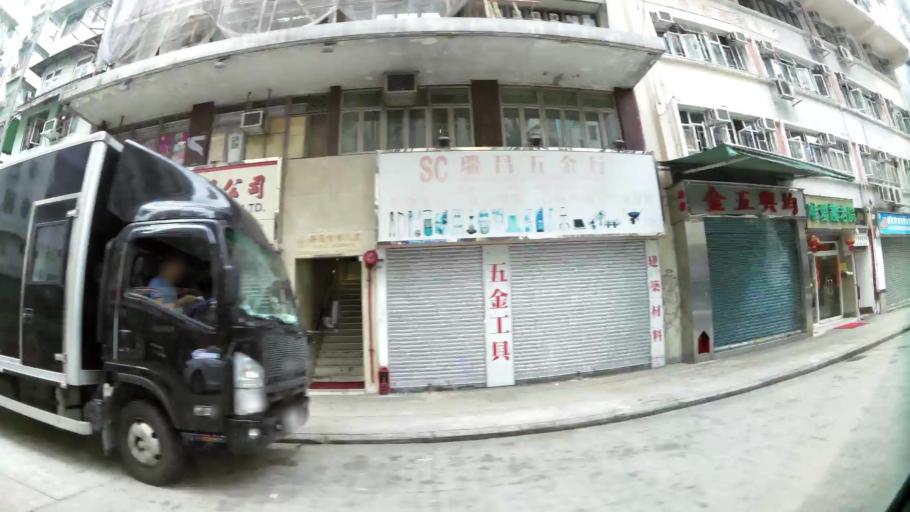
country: HK
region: Kowloon City
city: Kowloon
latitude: 22.3144
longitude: 114.1686
